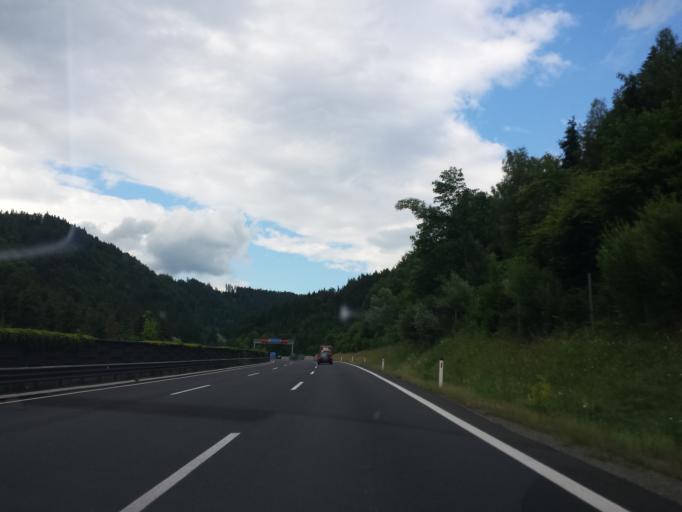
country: AT
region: Styria
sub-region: Politischer Bezirk Bruck-Muerzzuschlag
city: Bruck an der Mur
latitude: 47.4197
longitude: 15.2950
